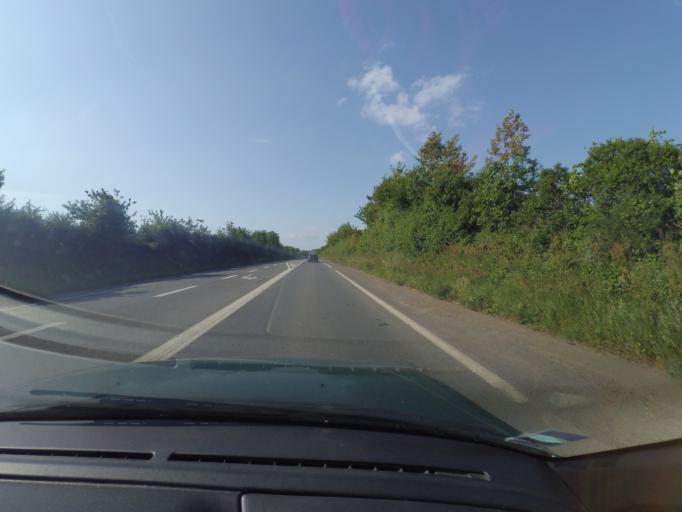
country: FR
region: Pays de la Loire
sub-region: Departement de la Vendee
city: Moutiers-les-Mauxfaits
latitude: 46.5196
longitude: -1.4322
